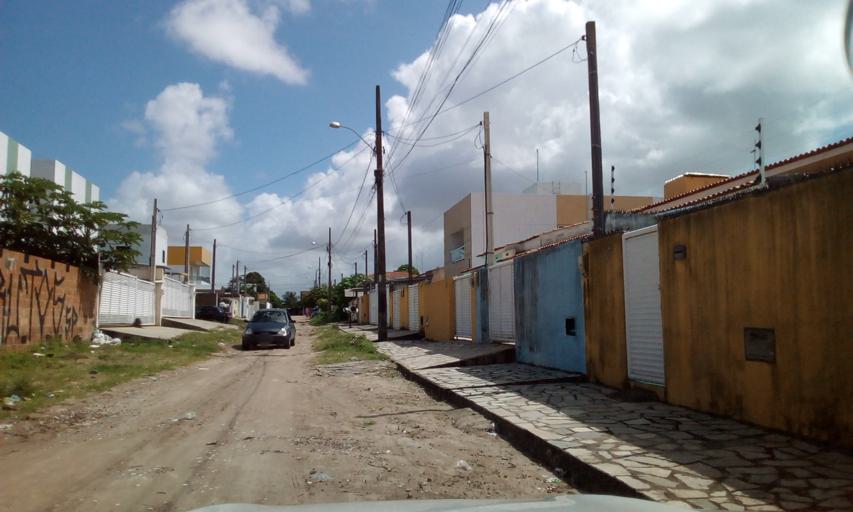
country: BR
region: Paraiba
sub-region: Conde
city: Conde
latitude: -7.2174
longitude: -34.8310
